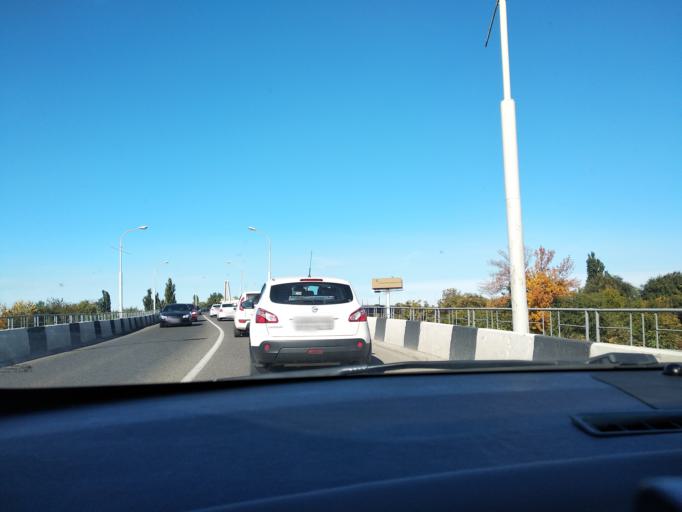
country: RU
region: Adygeya
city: Yablonovskiy
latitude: 44.9928
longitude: 38.9559
